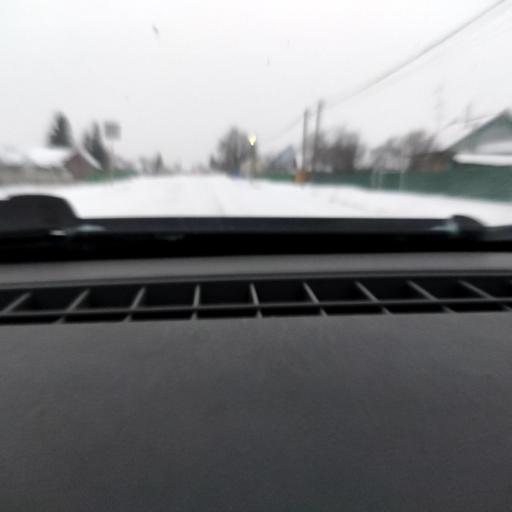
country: RU
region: Bashkortostan
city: Ulukulevo
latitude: 54.3879
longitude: 56.4459
